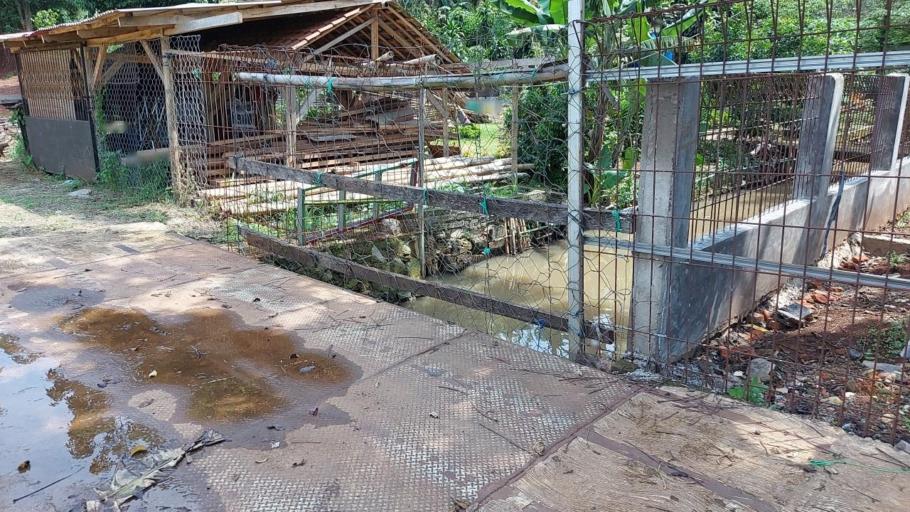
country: ID
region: West Java
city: Cibinong
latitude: -6.4680
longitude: 106.8084
